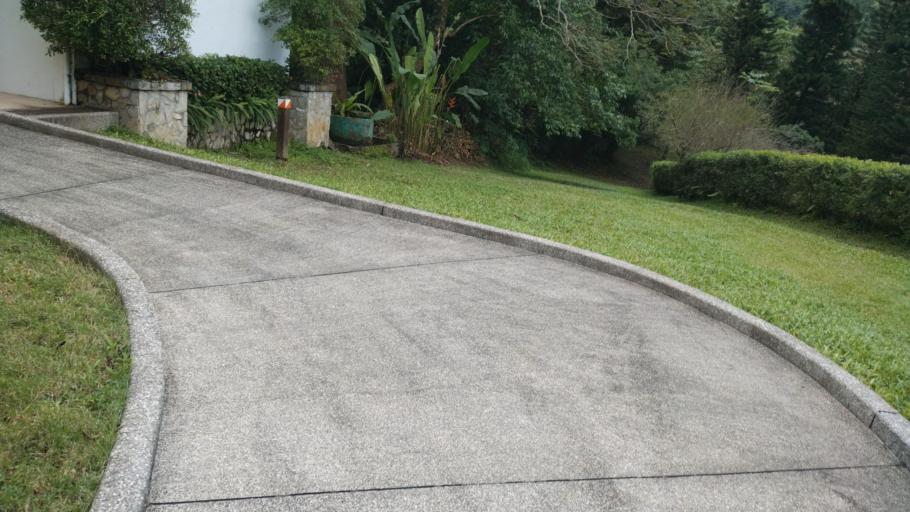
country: TW
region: Taiwan
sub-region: Hualien
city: Hualian
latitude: 23.9184
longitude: 121.5009
